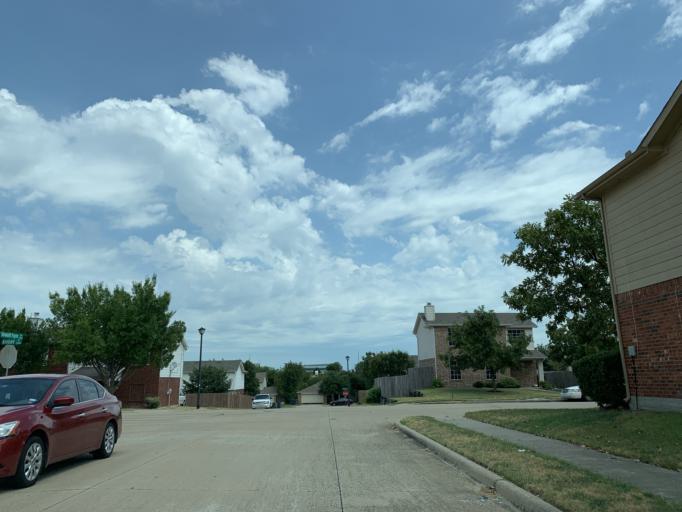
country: US
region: Texas
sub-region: Dallas County
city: DeSoto
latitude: 32.6584
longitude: -96.8117
